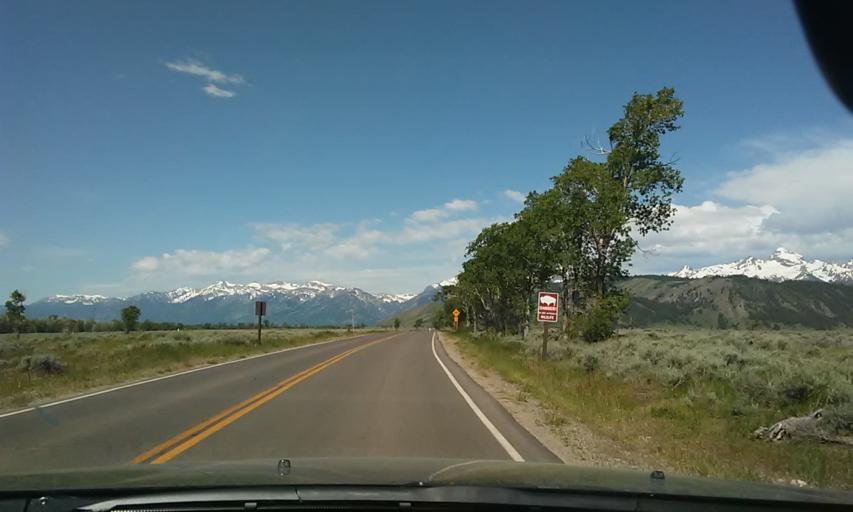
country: US
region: Wyoming
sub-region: Teton County
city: Jackson
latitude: 43.6252
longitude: -110.6307
